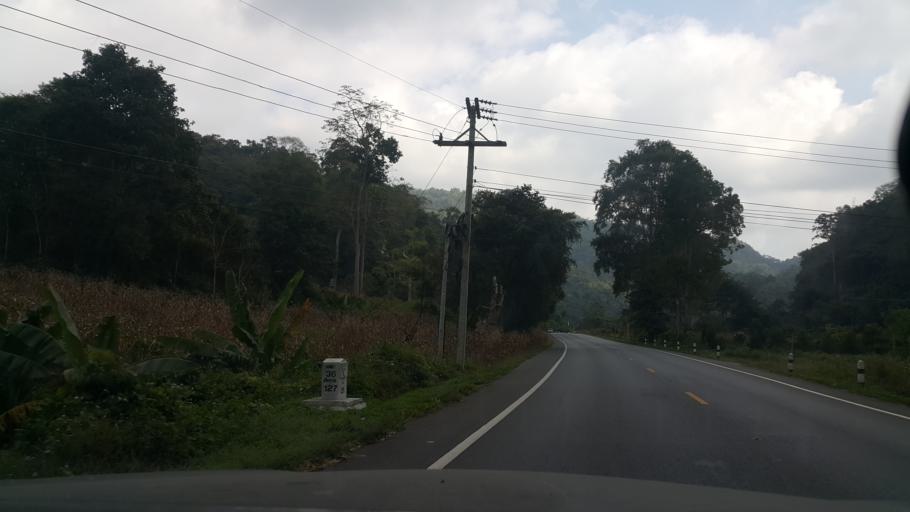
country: TH
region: Lampang
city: Wang Nuea
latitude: 19.0646
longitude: 99.7465
